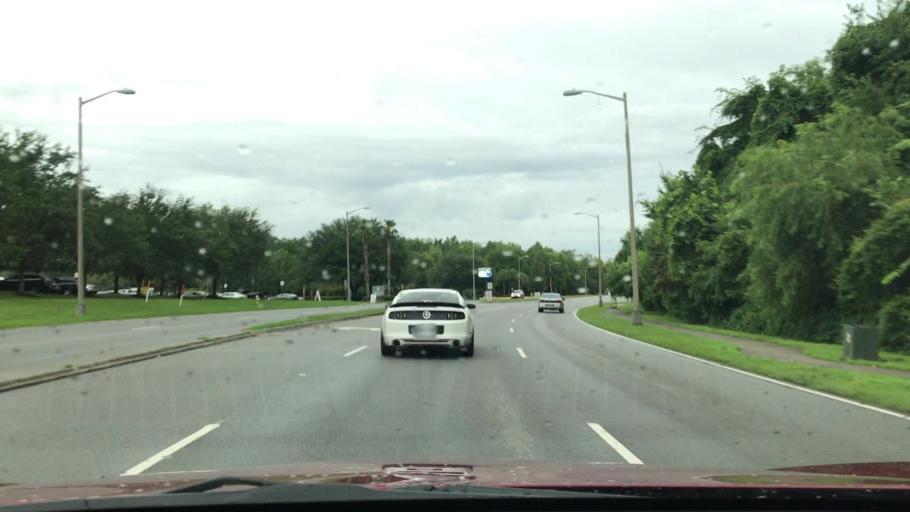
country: US
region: South Carolina
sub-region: Charleston County
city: North Charleston
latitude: 32.8672
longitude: -80.0189
